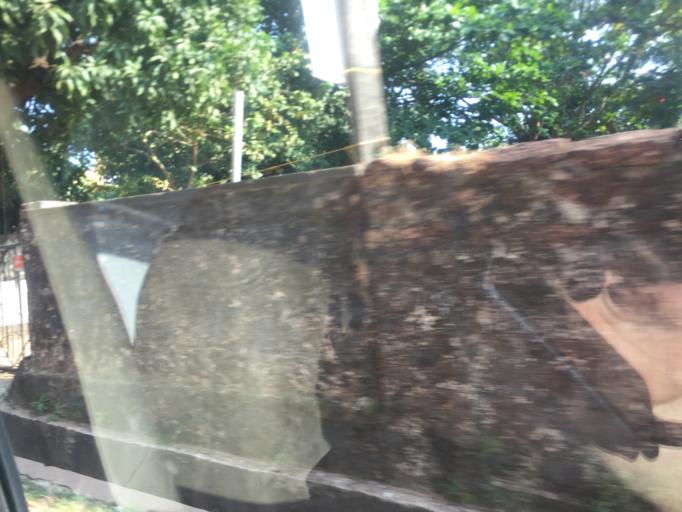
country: IN
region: Karnataka
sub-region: Dakshina Kannada
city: Ullal
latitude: 12.8482
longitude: 74.8389
